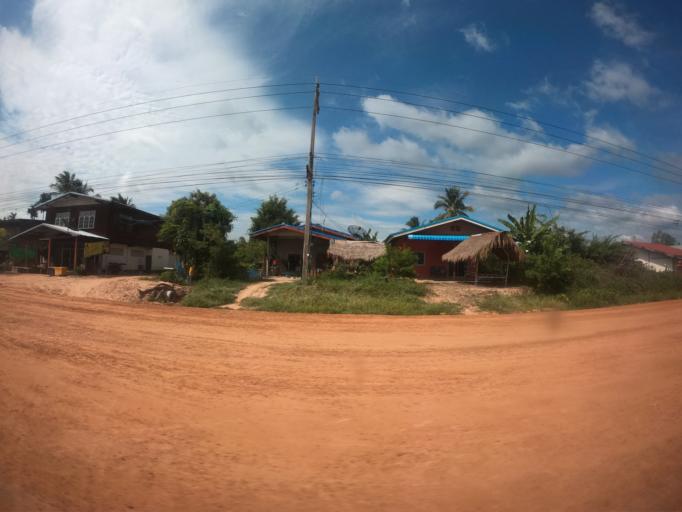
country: TH
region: Surin
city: Kap Choeng
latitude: 14.4608
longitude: 103.6581
